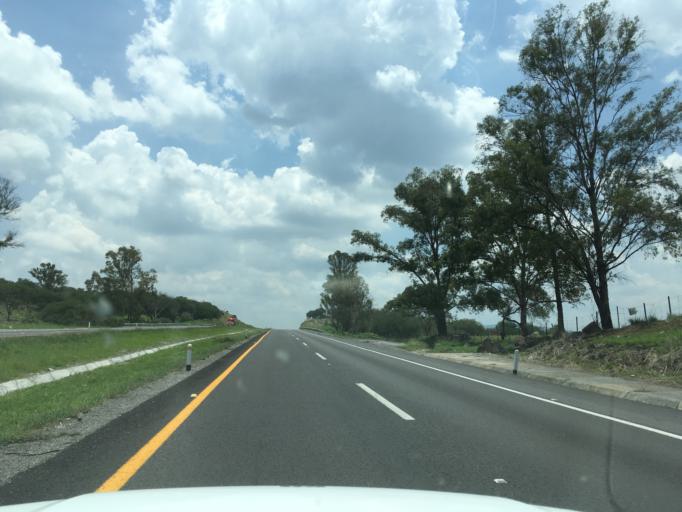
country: MX
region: Jalisco
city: Ocotlan
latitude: 20.4363
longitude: -102.8017
